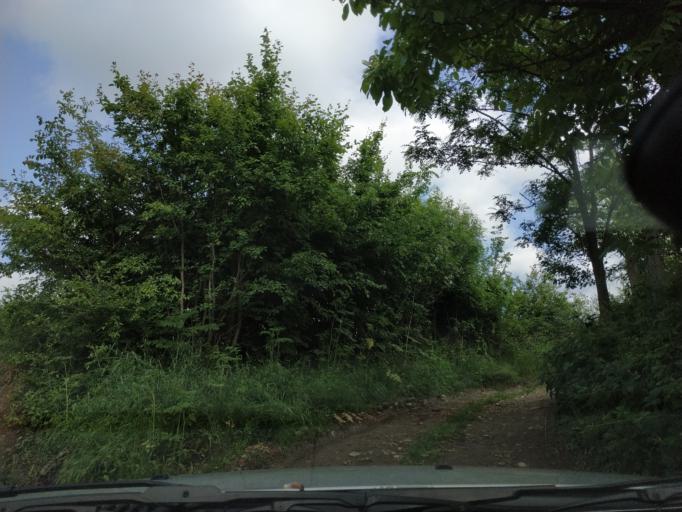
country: RS
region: Central Serbia
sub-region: Nisavski Okrug
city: Aleksinac
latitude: 43.4259
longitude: 21.5888
